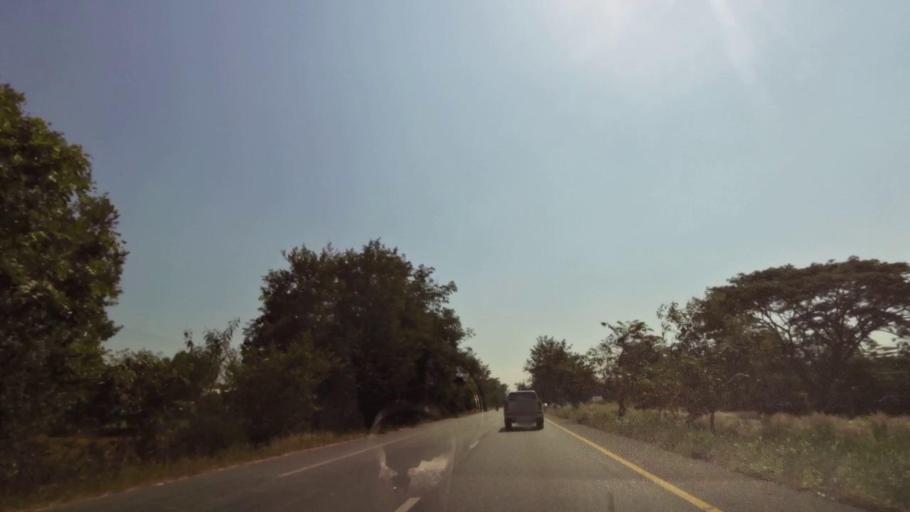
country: TH
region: Nakhon Sawan
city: Kao Liao
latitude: 15.8556
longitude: 100.1170
